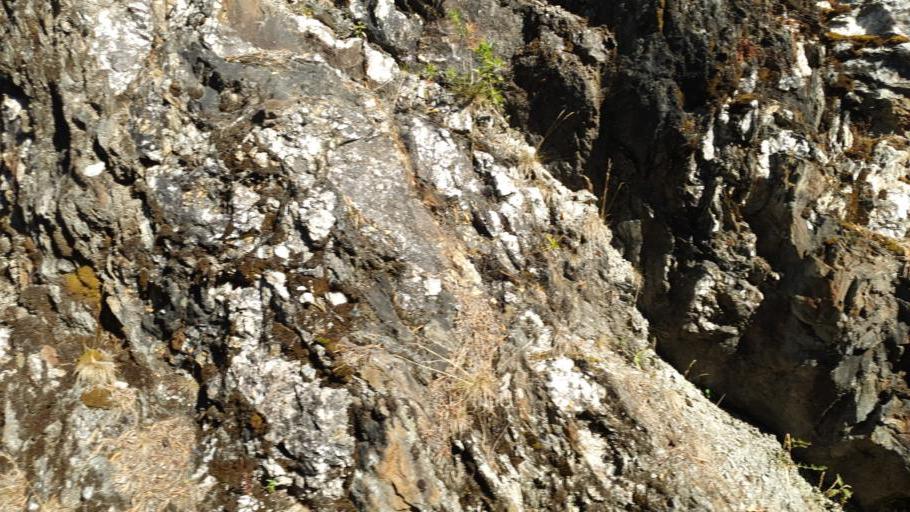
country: NO
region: Sor-Trondelag
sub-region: Meldal
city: Meldal
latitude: 63.1719
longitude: 9.7487
